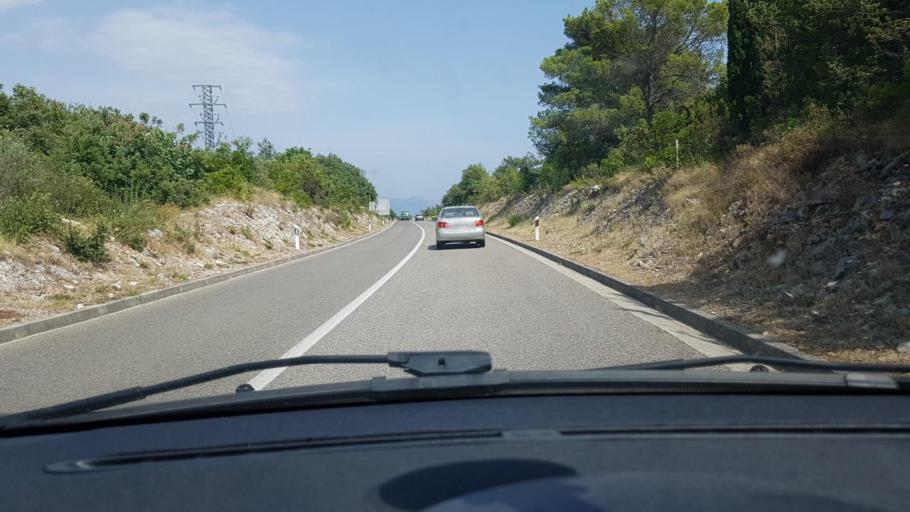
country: HR
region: Dubrovacko-Neretvanska
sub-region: Grad Korcula
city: Zrnovo
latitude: 42.9449
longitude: 17.1131
